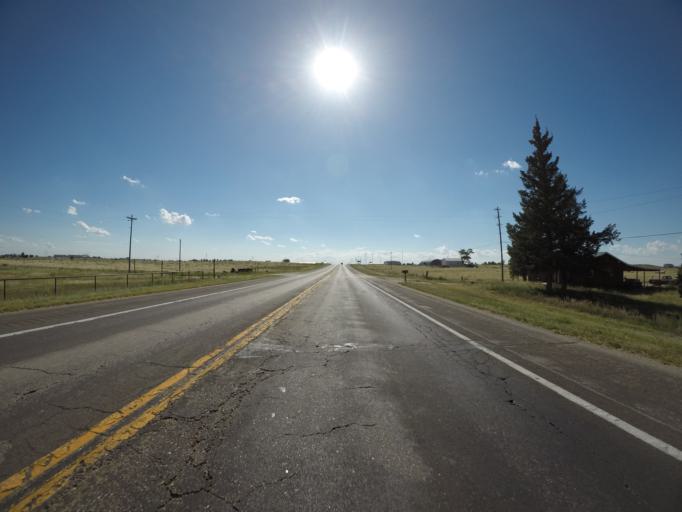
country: US
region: Colorado
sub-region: Logan County
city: Sterling
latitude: 40.6237
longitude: -103.2718
